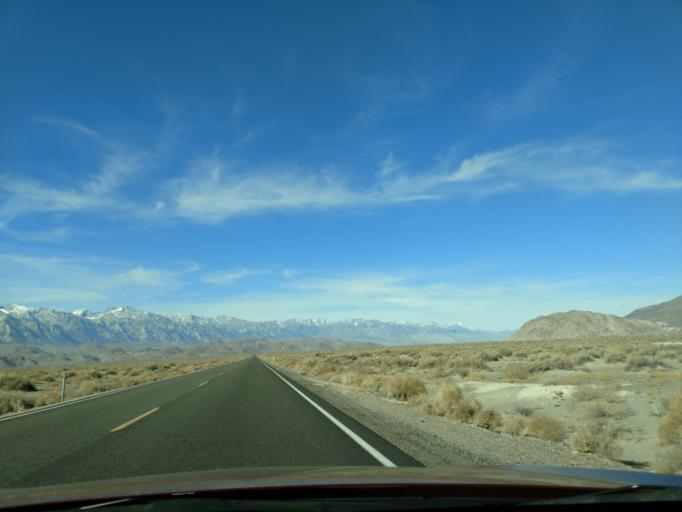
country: US
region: California
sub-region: Inyo County
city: Lone Pine
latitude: 36.5571
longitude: -117.9625
